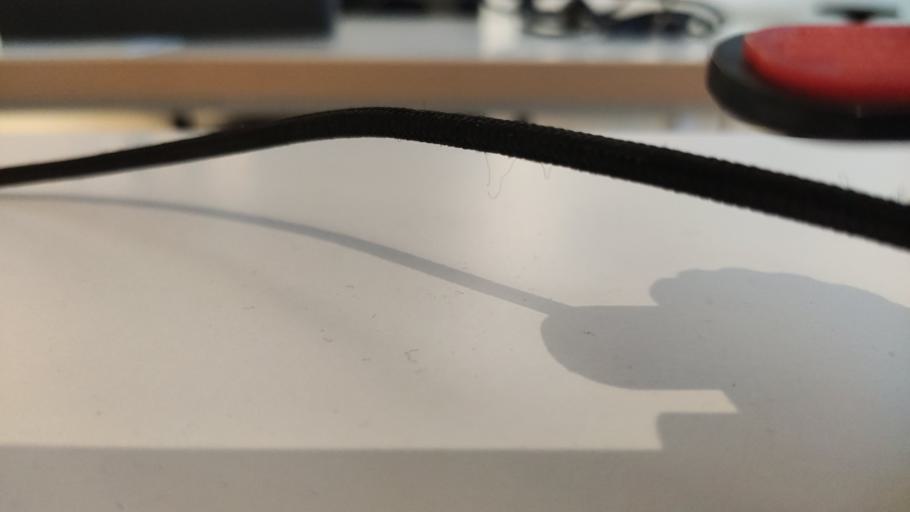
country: RU
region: Moskovskaya
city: Novopetrovskoye
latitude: 55.8613
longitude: 36.3848
